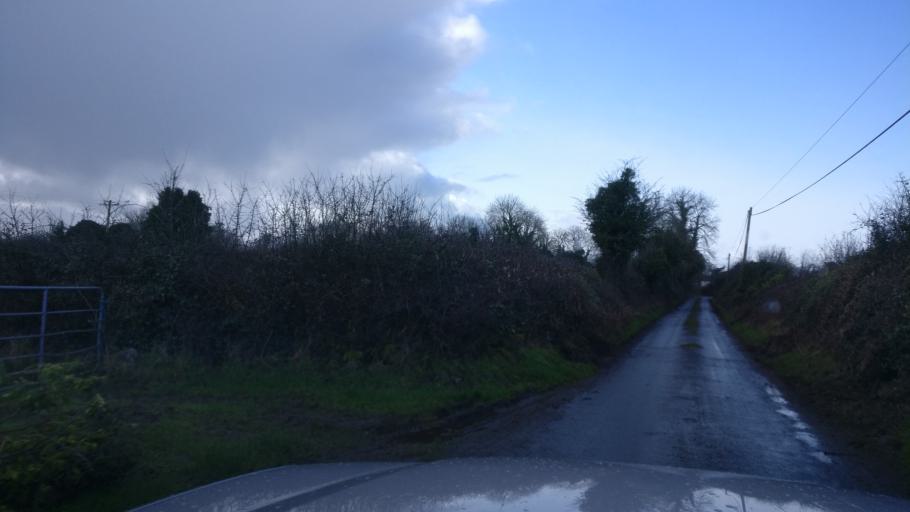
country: IE
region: Connaught
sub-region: County Galway
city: Oranmore
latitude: 53.2584
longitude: -8.8946
